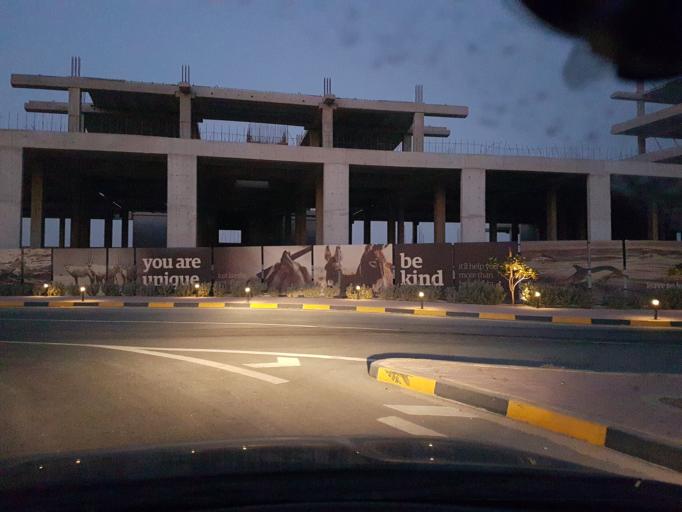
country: BH
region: Central Governorate
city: Dar Kulayb
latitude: 26.0138
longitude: 50.5128
